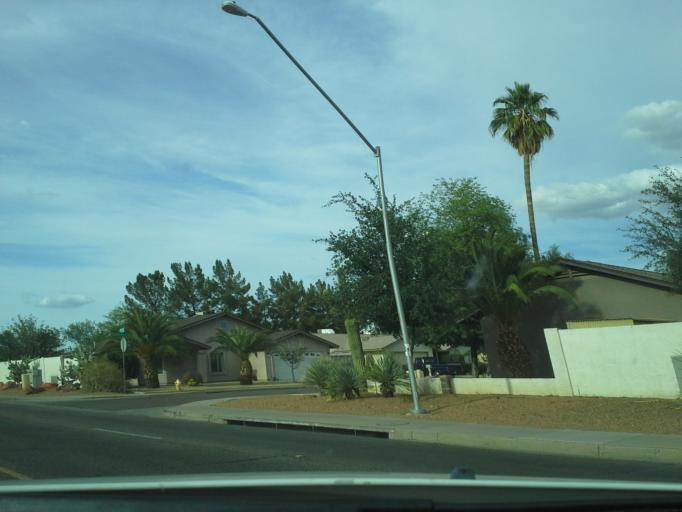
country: US
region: Arizona
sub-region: Maricopa County
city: Peoria
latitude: 33.6356
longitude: -112.2027
